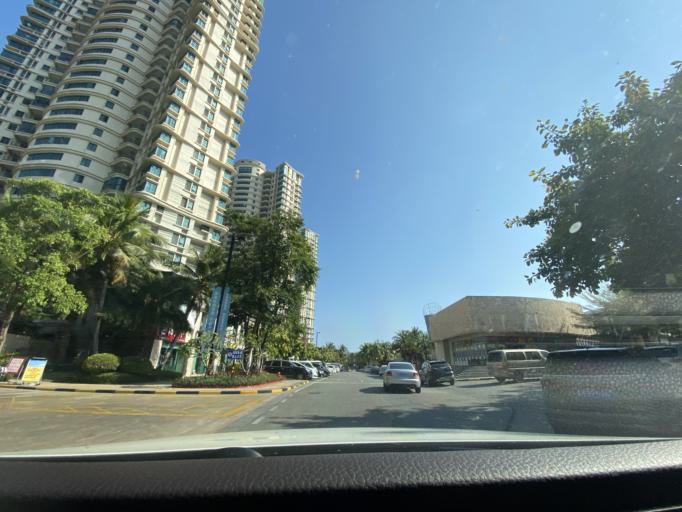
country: CN
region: Hainan
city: Yingzhou
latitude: 18.4102
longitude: 109.8749
